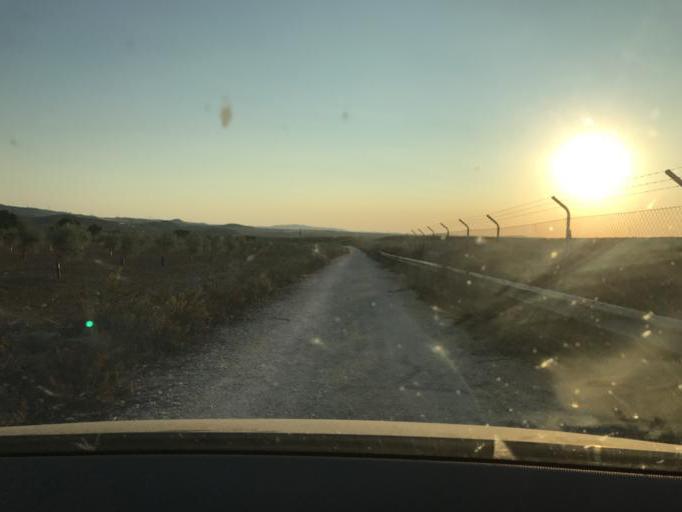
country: ES
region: Andalusia
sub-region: Provincia de Sevilla
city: Osuna
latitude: 37.2302
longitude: -5.0512
